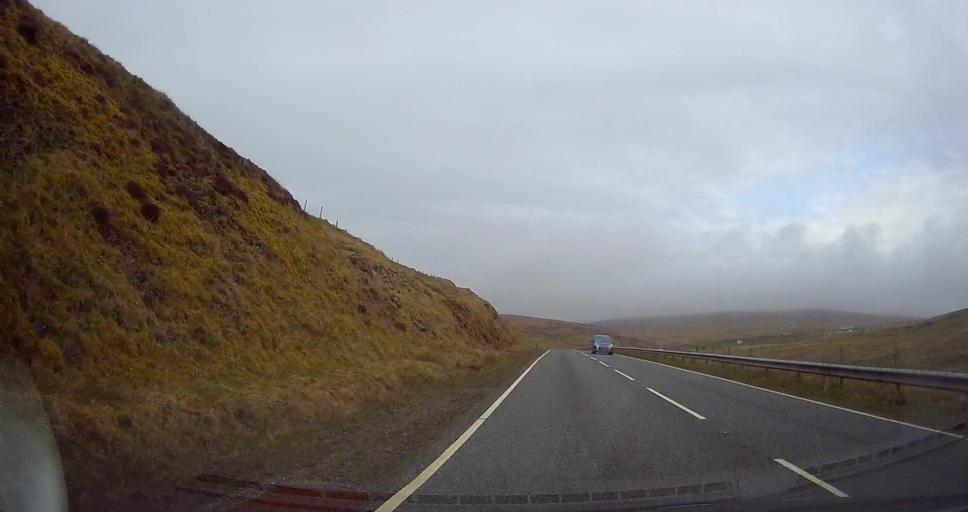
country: GB
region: Scotland
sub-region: Shetland Islands
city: Sandwick
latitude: 59.9987
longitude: -1.2796
